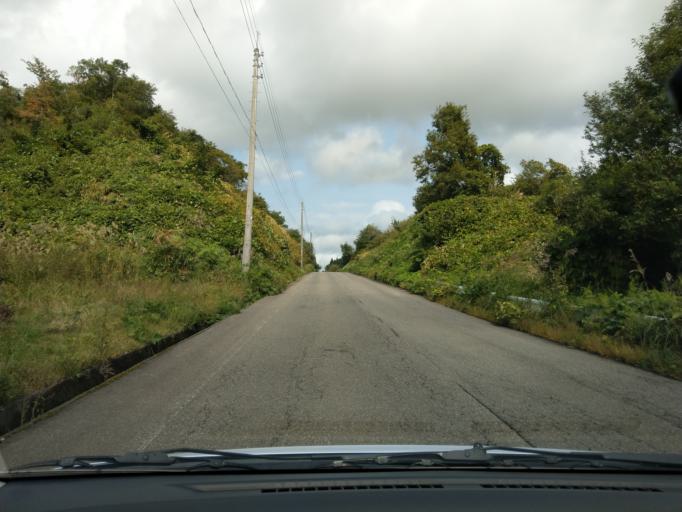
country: JP
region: Akita
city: Omagari
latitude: 39.4492
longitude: 140.3230
